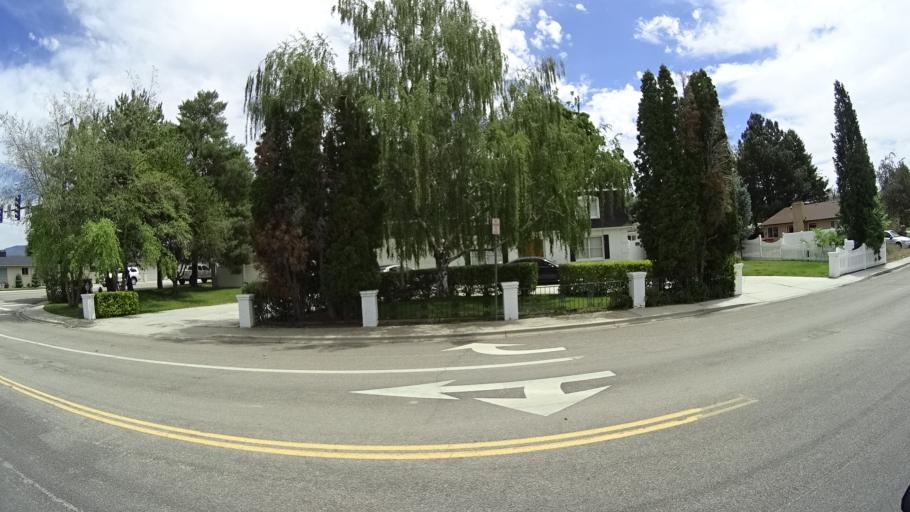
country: US
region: Idaho
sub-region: Ada County
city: Garden City
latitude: 43.6435
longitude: -116.2779
